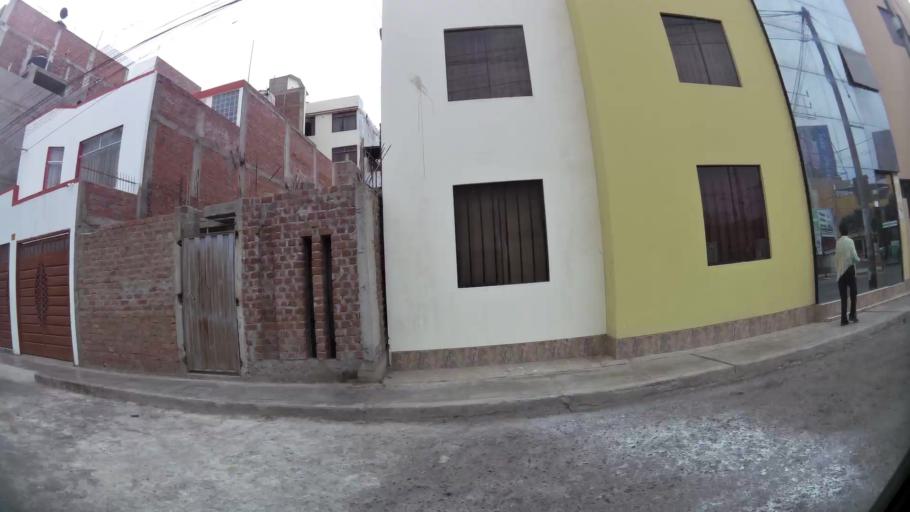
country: PE
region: La Libertad
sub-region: Provincia de Trujillo
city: Buenos Aires
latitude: -8.1314
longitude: -79.0343
